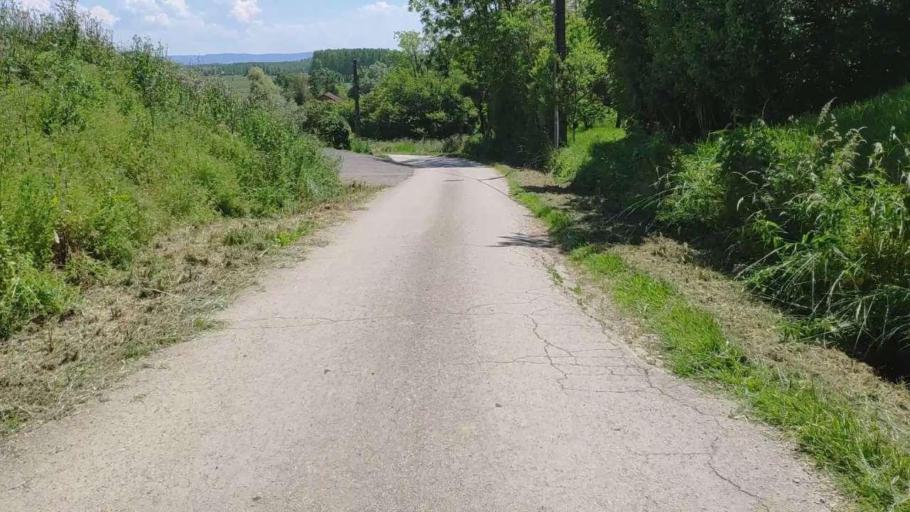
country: FR
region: Franche-Comte
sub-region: Departement du Jura
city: Bletterans
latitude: 46.7407
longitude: 5.3862
